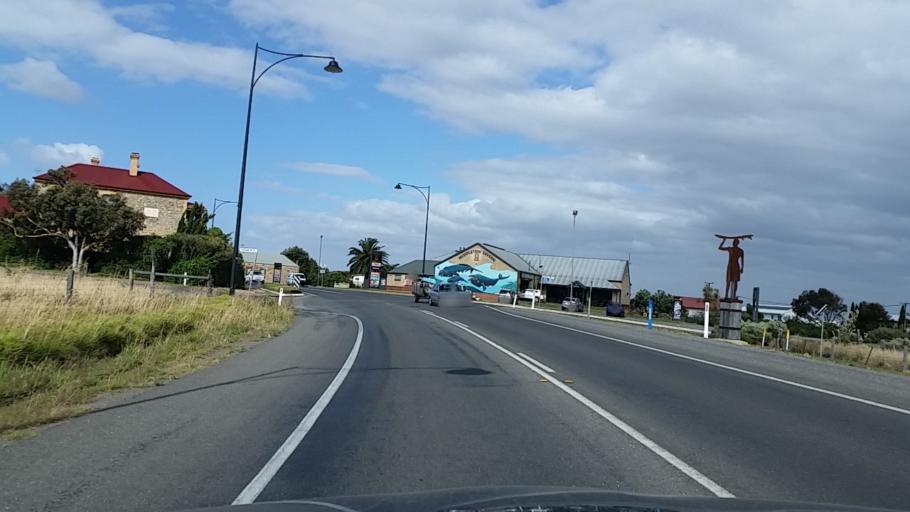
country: AU
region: South Australia
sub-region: Alexandrina
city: Port Elliot
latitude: -35.5109
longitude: 138.7046
